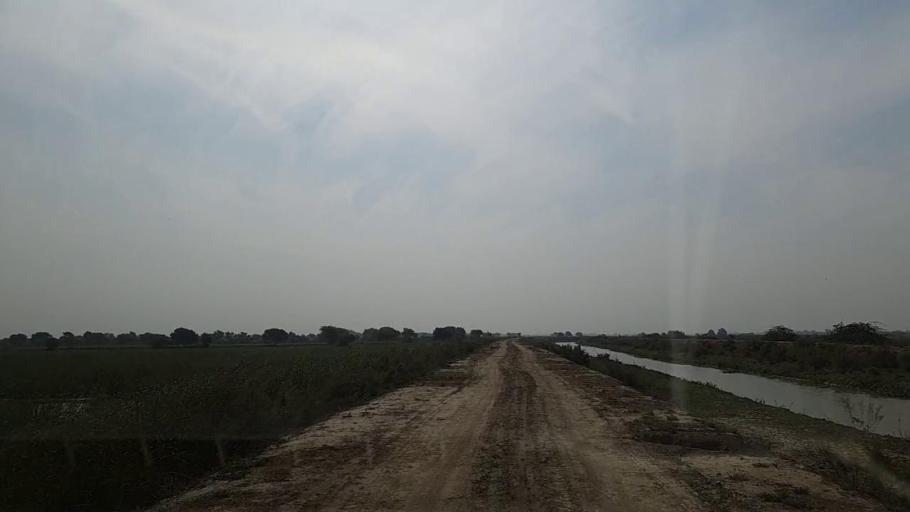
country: PK
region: Sindh
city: Mirpur Batoro
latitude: 24.6653
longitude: 68.2503
